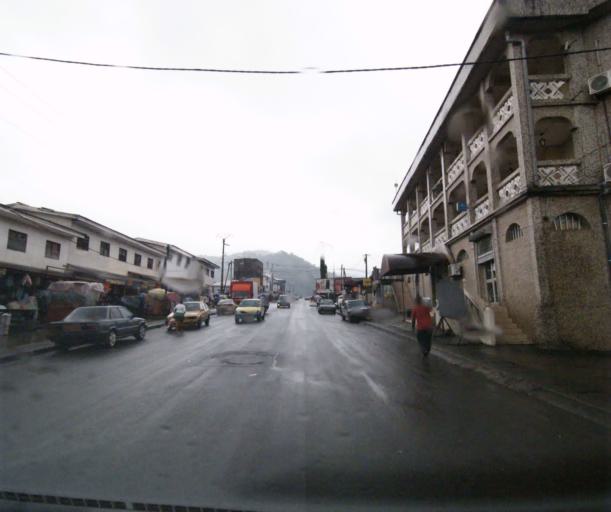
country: CM
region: South-West Province
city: Limbe
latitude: 4.0102
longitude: 9.2150
